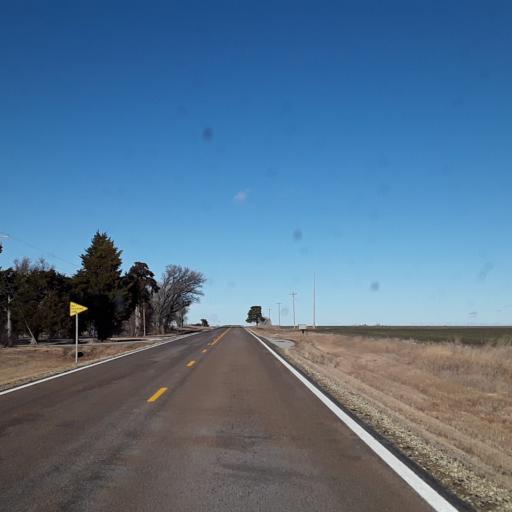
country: US
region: Kansas
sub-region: Mitchell County
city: Beloit
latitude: 39.3441
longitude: -98.1161
